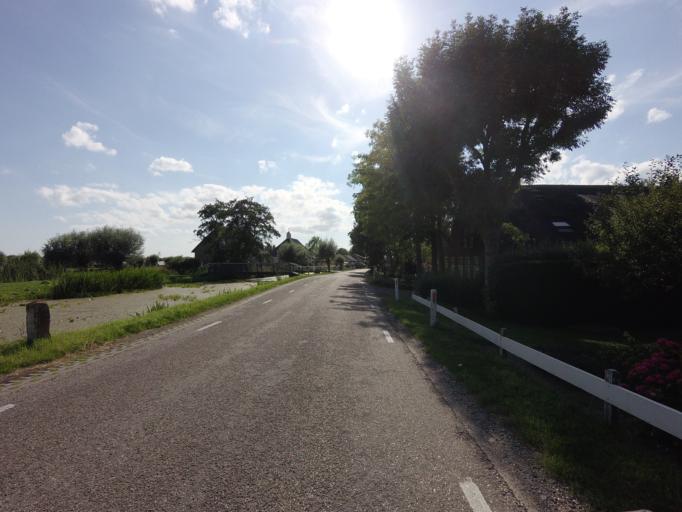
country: NL
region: Utrecht
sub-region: Gemeente Lopik
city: Lopik
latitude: 51.9766
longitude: 4.9628
